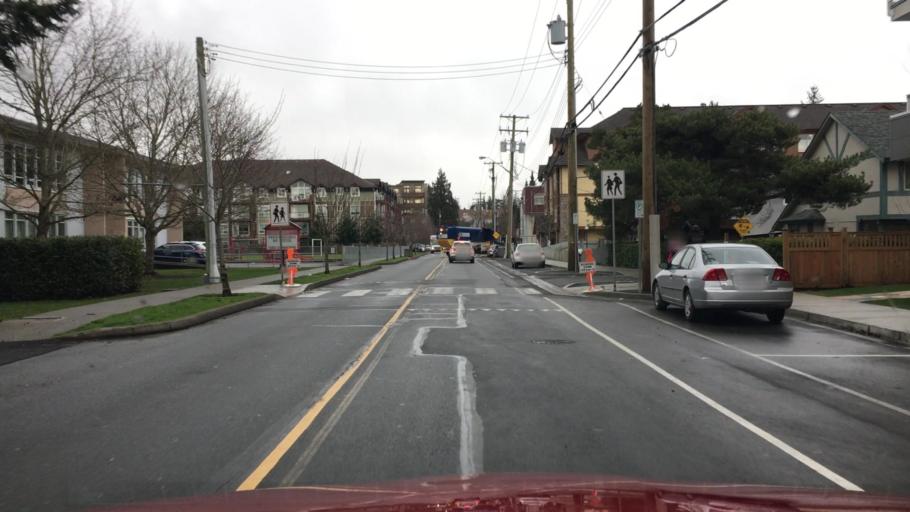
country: CA
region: British Columbia
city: Langford
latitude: 48.4517
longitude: -123.5049
